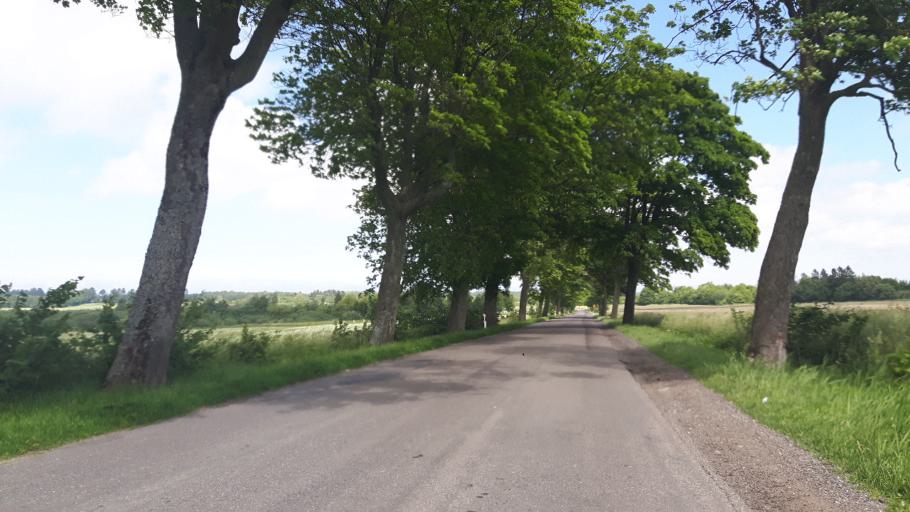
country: PL
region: Pomeranian Voivodeship
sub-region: Powiat slupski
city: Ustka
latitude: 54.5475
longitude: 16.8290
